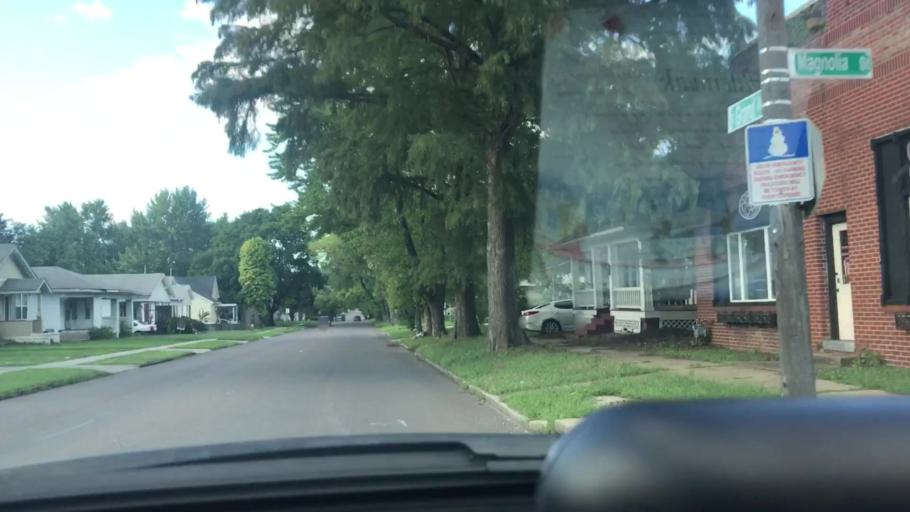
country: US
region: Missouri
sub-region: Pettis County
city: Sedalia
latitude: 38.6984
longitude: -93.2367
